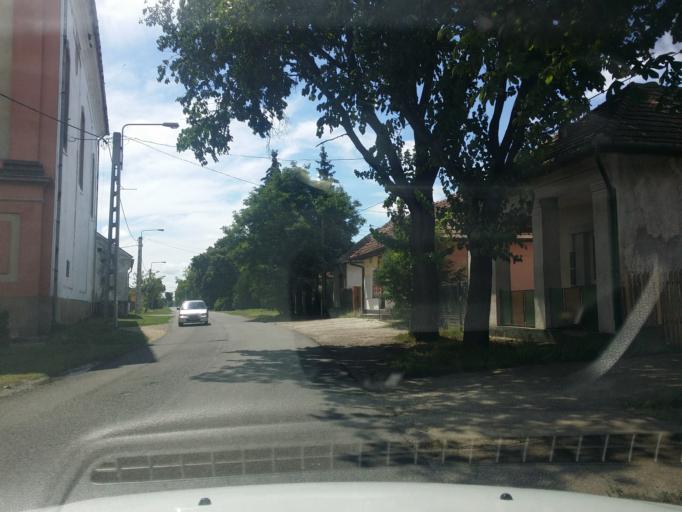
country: HU
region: Heves
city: Tiszanana
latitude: 47.5884
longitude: 20.5965
